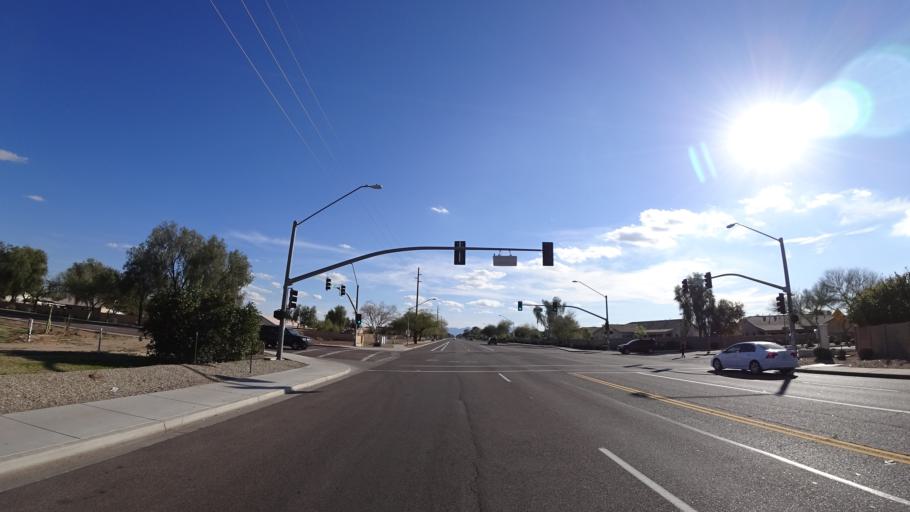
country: US
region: Arizona
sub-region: Maricopa County
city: Peoria
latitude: 33.5307
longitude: -112.2376
